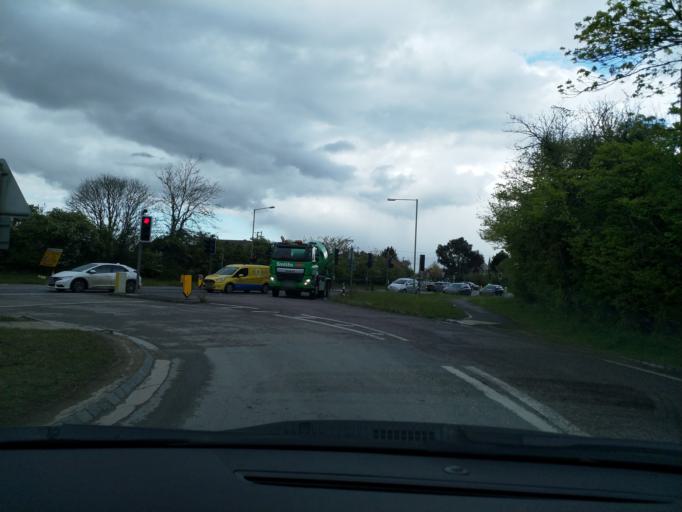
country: GB
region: England
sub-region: Oxfordshire
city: Eynsham
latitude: 51.7894
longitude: -1.3499
